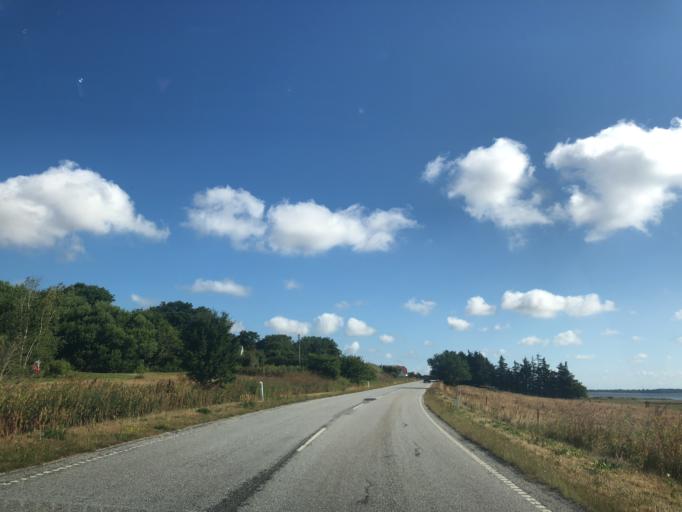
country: DK
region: North Denmark
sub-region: Morso Kommune
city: Nykobing Mors
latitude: 56.9859
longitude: 8.9104
